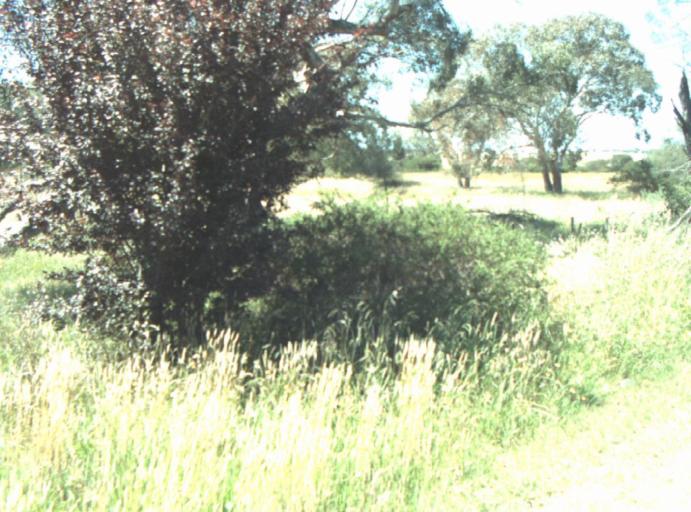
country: AU
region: Victoria
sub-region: Greater Geelong
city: Breakwater
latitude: -38.2344
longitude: 144.3539
